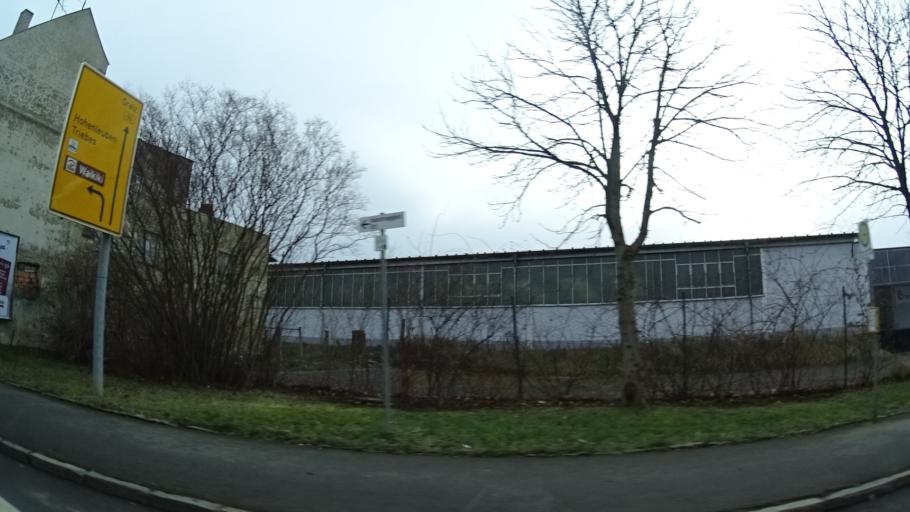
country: DE
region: Thuringia
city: Zeulenroda
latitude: 50.6562
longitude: 11.9941
